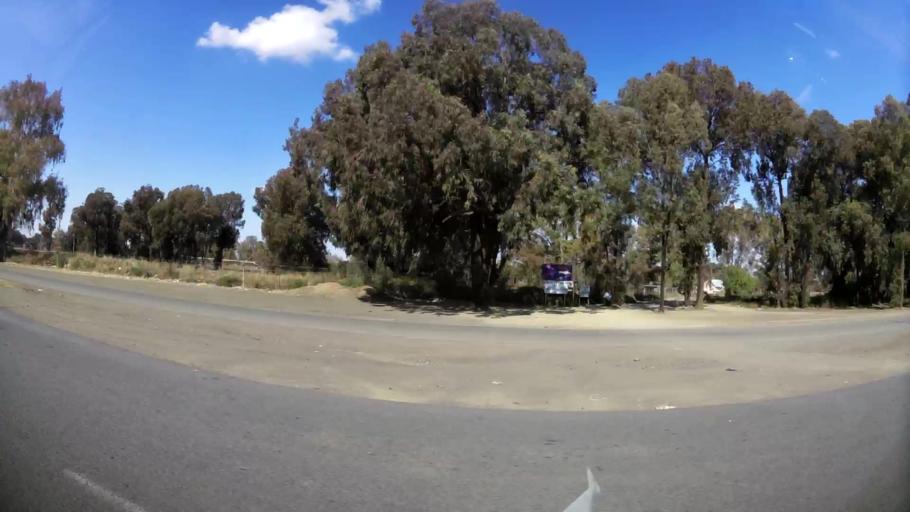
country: ZA
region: Orange Free State
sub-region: Mangaung Metropolitan Municipality
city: Bloemfontein
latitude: -29.1167
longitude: 26.2398
